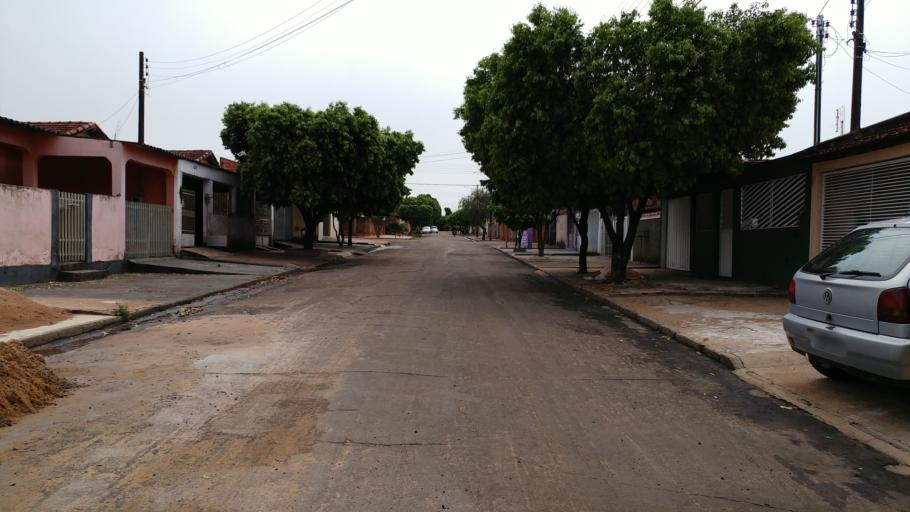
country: BR
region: Sao Paulo
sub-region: Paraguacu Paulista
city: Paraguacu Paulista
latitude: -22.4347
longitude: -50.5825
